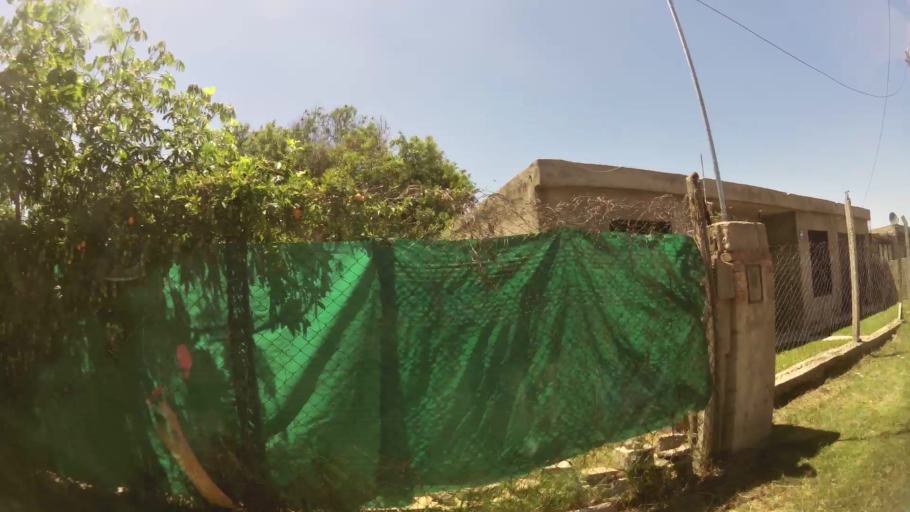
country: AR
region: Cordoba
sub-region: Departamento de Capital
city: Cordoba
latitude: -31.4383
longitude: -64.1222
